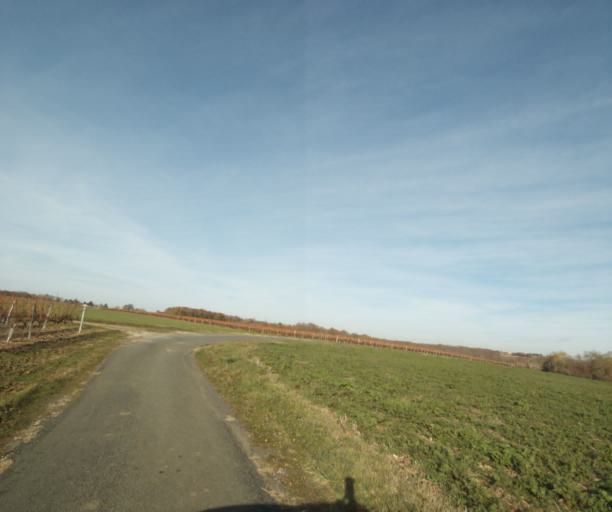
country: FR
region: Poitou-Charentes
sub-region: Departement de la Charente-Maritime
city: Chaniers
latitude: 45.7202
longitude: -0.5386
